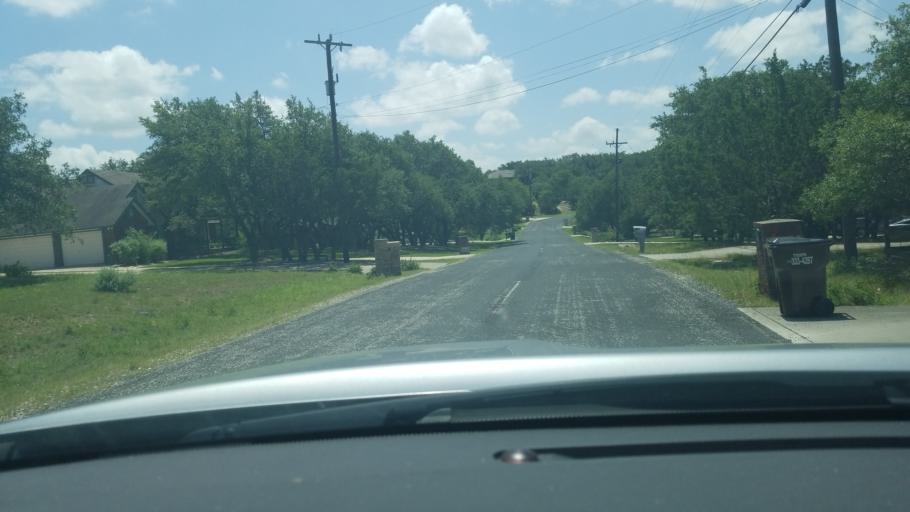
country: US
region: Texas
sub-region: Bexar County
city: Timberwood Park
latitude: 29.6913
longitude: -98.4867
